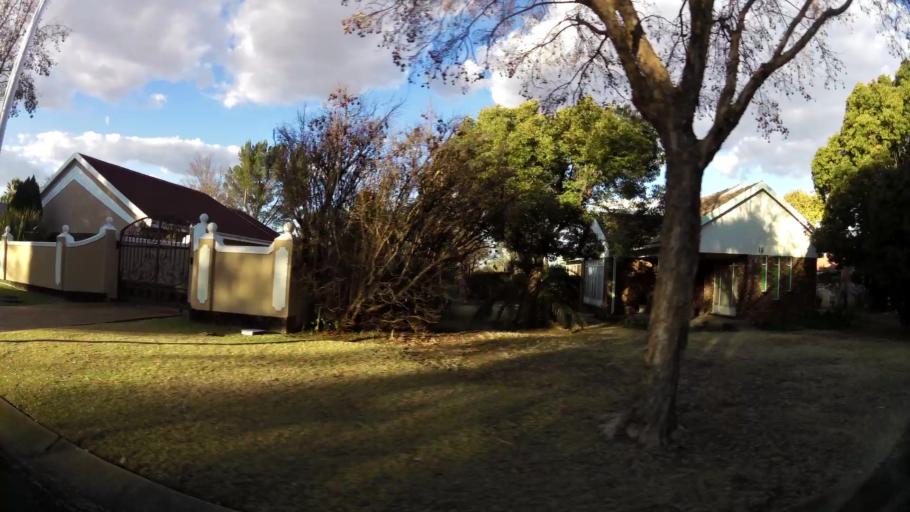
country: ZA
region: North-West
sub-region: Dr Kenneth Kaunda District Municipality
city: Potchefstroom
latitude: -26.7331
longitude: 27.0999
